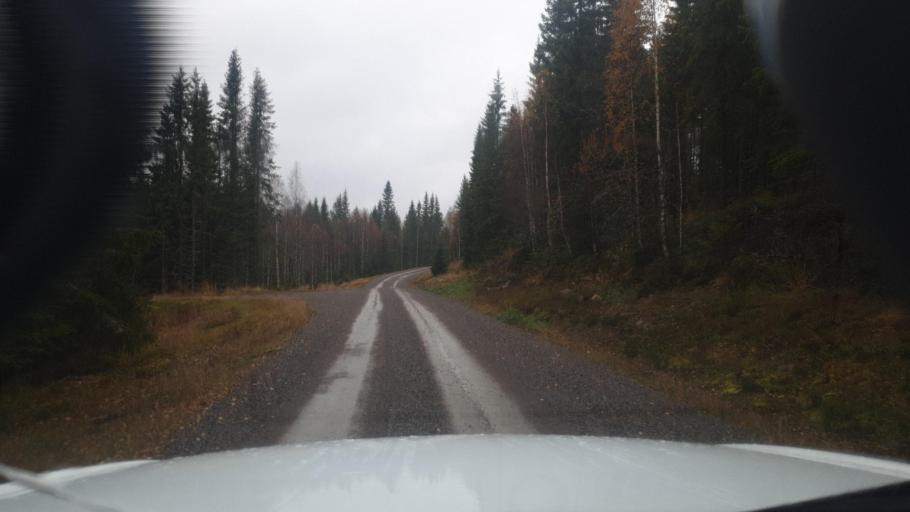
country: SE
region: Vaermland
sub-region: Eda Kommun
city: Charlottenberg
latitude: 60.0961
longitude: 12.6114
